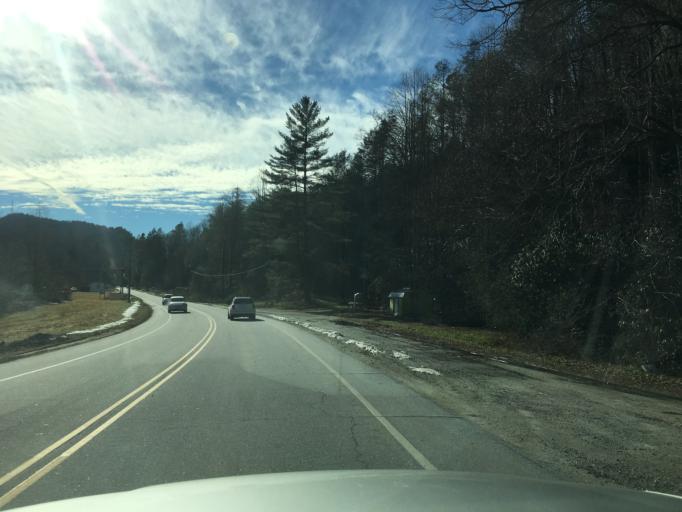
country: US
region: North Carolina
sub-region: Transylvania County
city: Brevard
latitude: 35.1474
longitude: -82.8333
